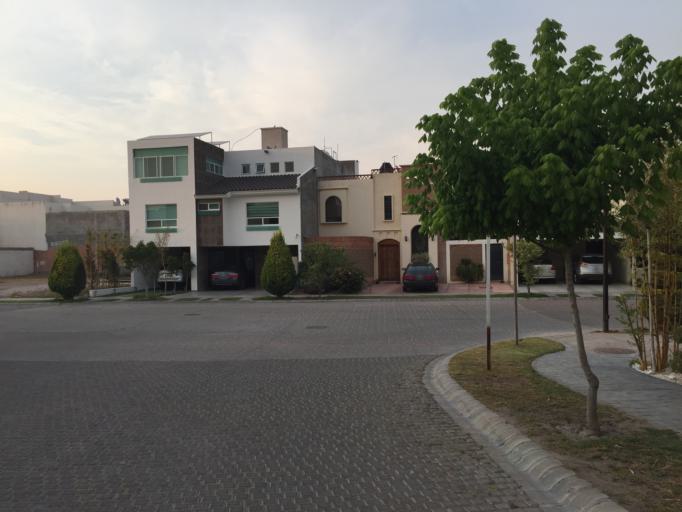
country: MX
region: Aguascalientes
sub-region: Aguascalientes
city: La Loma de los Negritos
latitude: 21.8474
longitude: -102.3556
